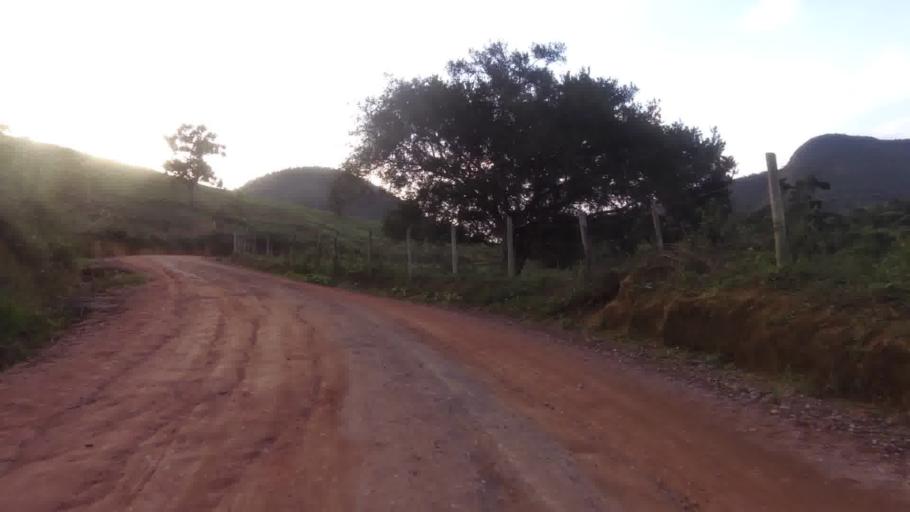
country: BR
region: Espirito Santo
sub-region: Guarapari
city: Guarapari
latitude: -20.6880
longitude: -40.6280
